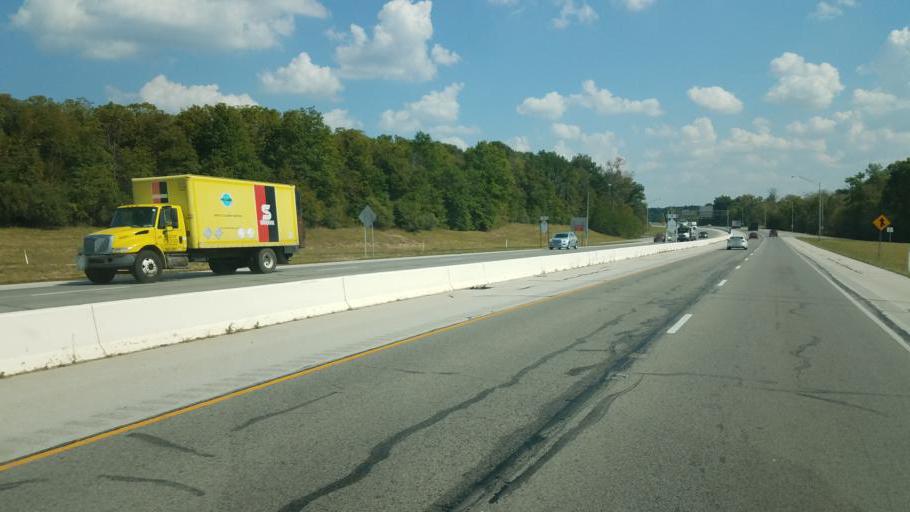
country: US
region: Indiana
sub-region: Allen County
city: Leo-Cedarville
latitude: 41.1585
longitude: -85.0594
